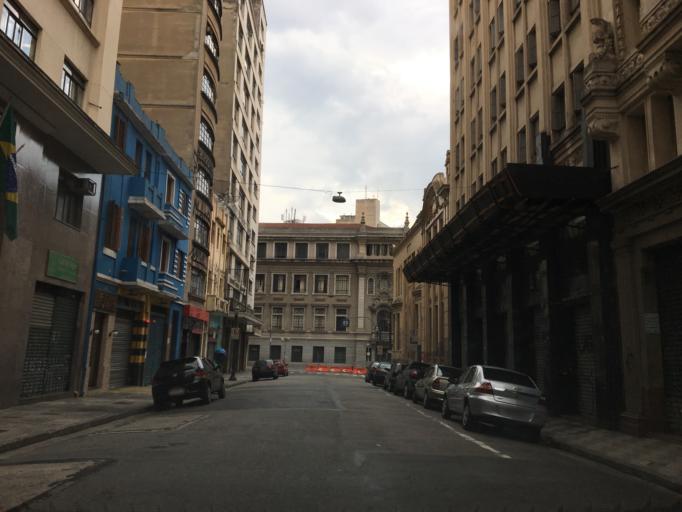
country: BR
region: Sao Paulo
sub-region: Sao Paulo
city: Sao Paulo
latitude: -23.5503
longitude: -46.6358
